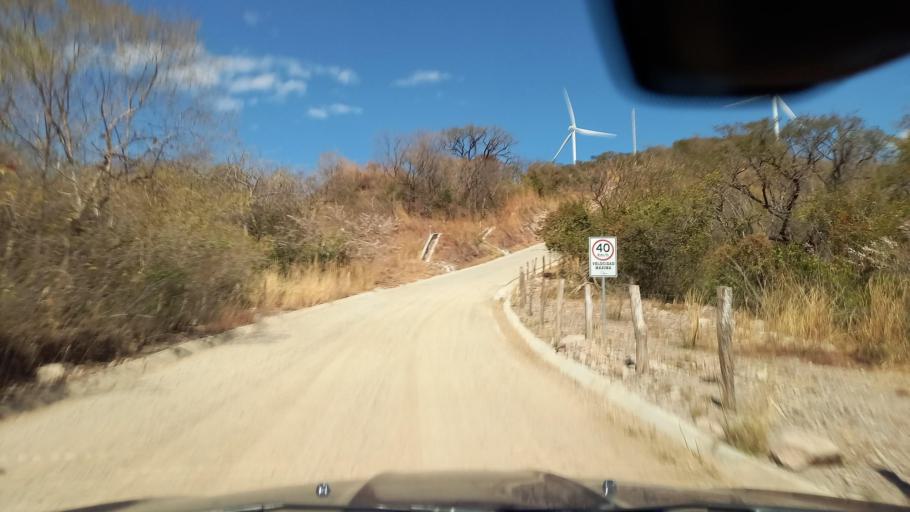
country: SV
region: Santa Ana
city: Metapan
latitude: 14.3613
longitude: -89.4814
